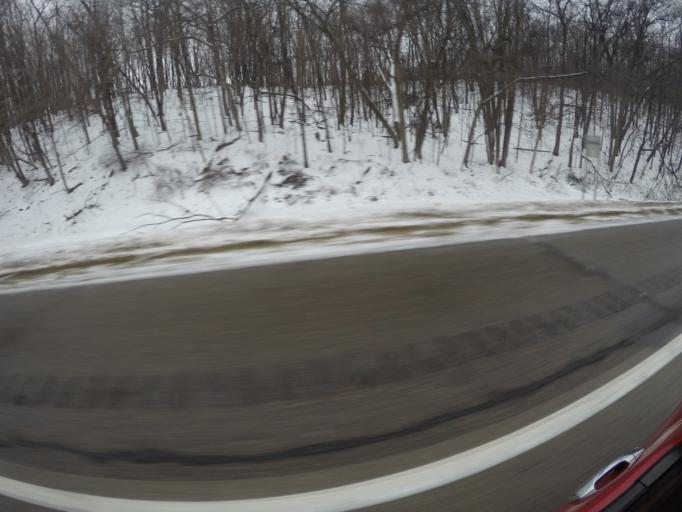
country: US
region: Minnesota
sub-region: Goodhue County
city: Cannon Falls
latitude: 44.4444
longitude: -92.8932
